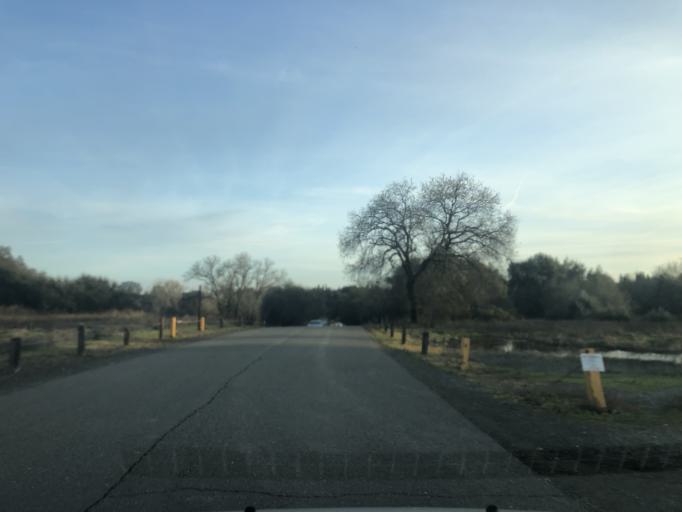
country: US
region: California
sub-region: Sacramento County
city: Gold River
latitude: 38.6360
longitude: -121.2352
